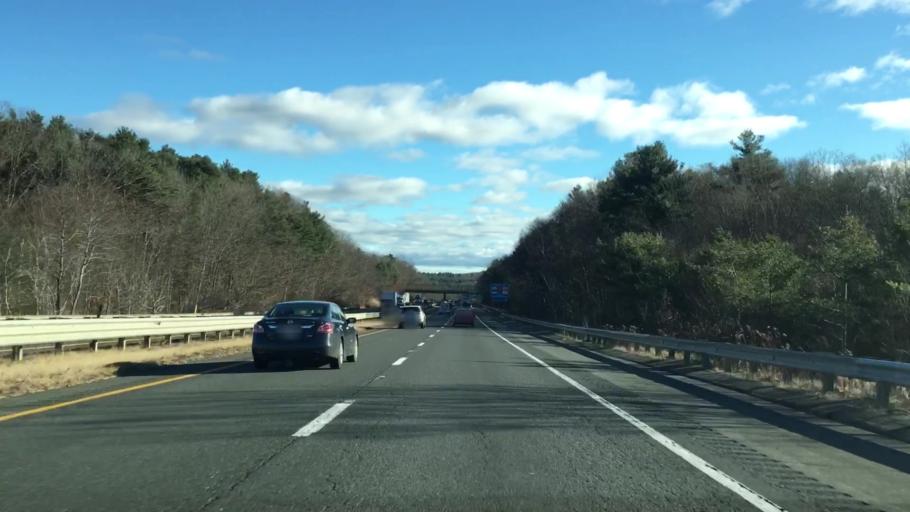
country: US
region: Massachusetts
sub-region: Worcester County
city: Fiskdale
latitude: 42.1346
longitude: -72.1010
